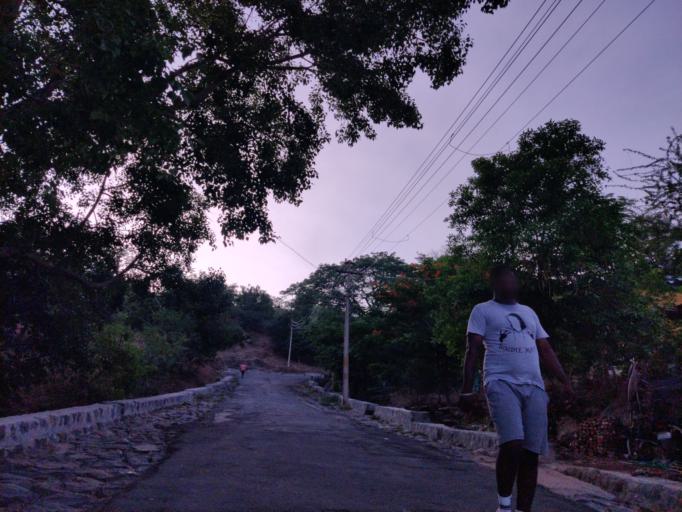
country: IN
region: Tamil Nadu
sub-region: Salem
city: Salem
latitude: 11.6218
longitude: 78.1497
